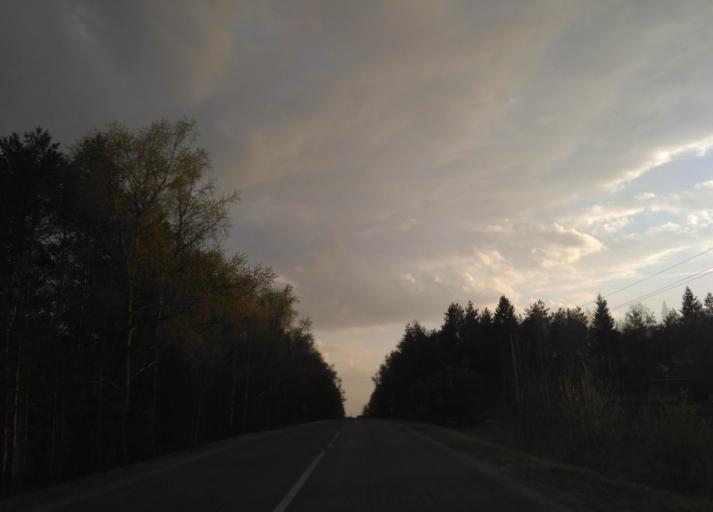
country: BY
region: Minsk
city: Loshnitsa
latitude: 54.4171
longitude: 28.6371
